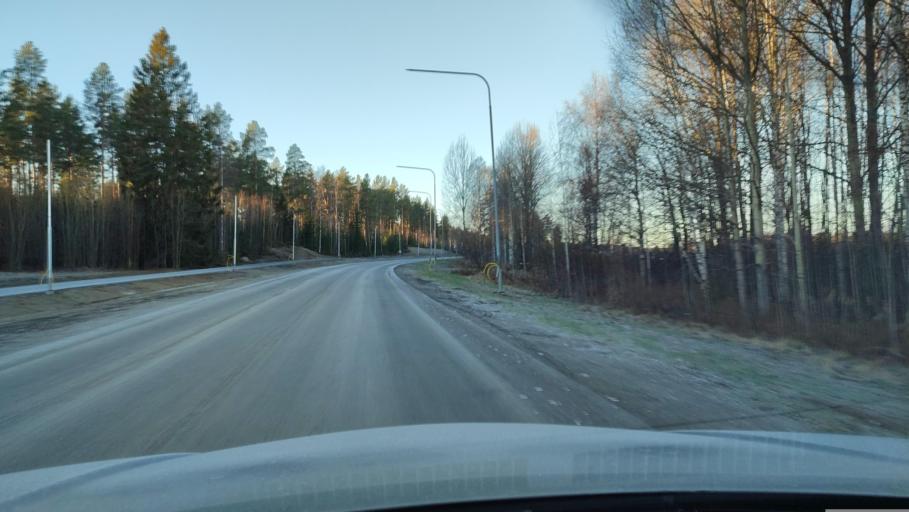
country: SE
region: Vaesterbotten
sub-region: Skelleftea Kommun
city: Skelleftea
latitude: 64.7398
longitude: 20.9416
